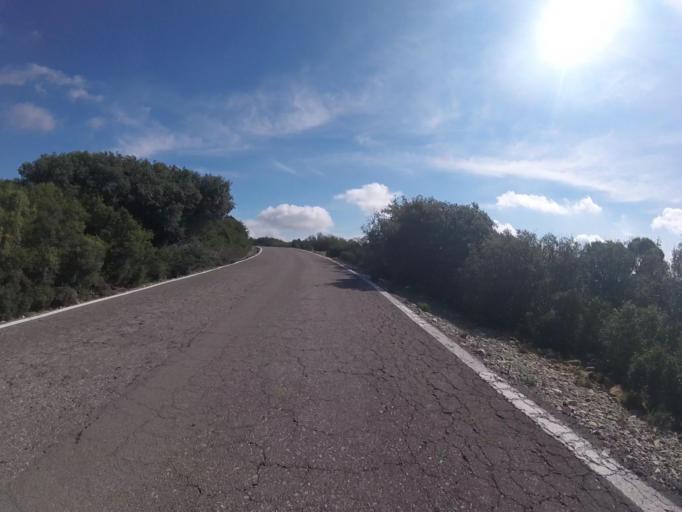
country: ES
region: Valencia
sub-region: Provincia de Castello
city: Albocasser
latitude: 40.3340
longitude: 0.0387
